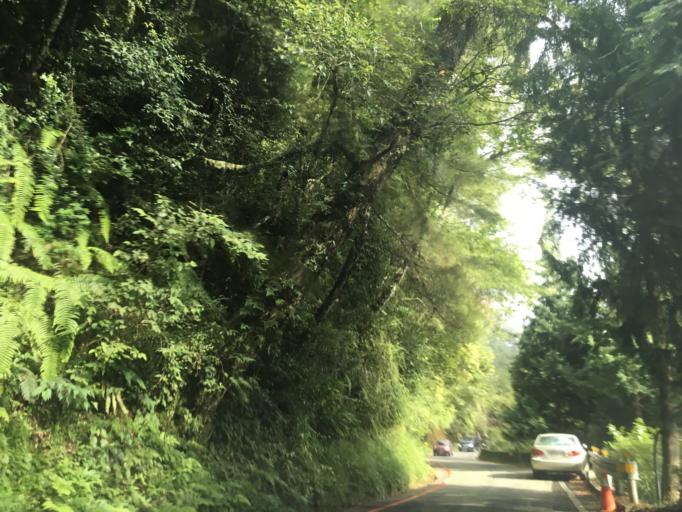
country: TW
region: Taiwan
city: Fengyuan
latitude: 24.2345
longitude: 120.9585
